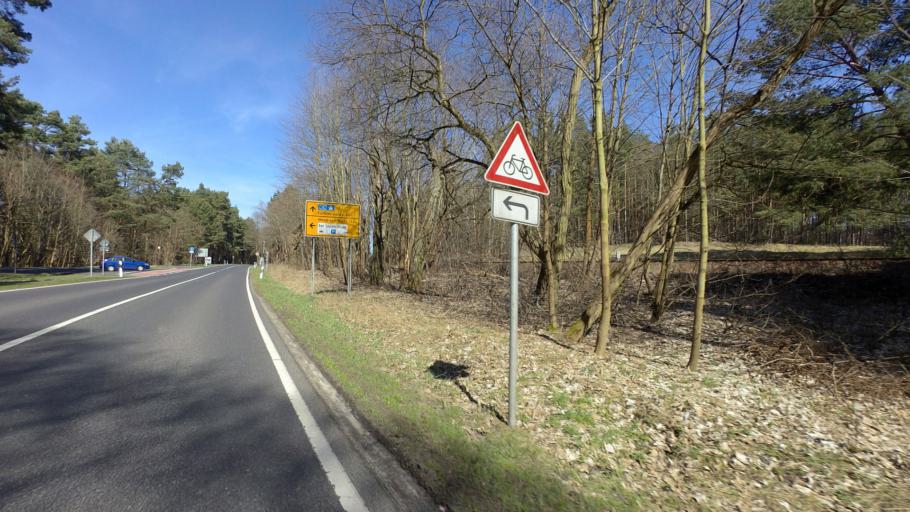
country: DE
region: Brandenburg
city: Bad Saarow
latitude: 52.3060
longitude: 14.0622
